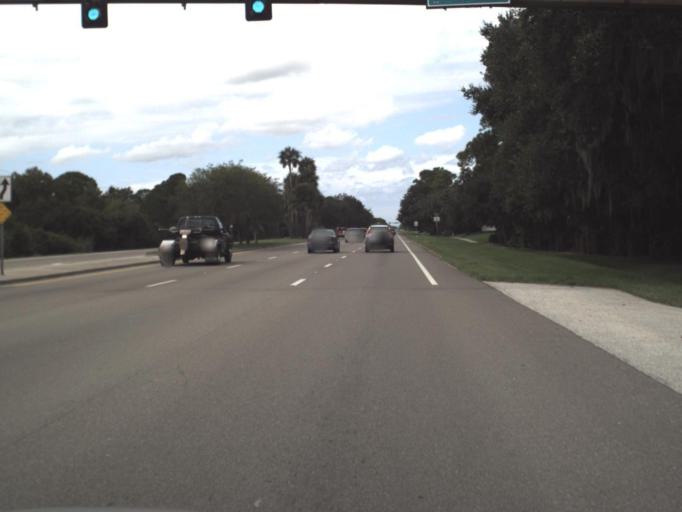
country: US
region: Florida
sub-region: Sarasota County
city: Desoto Lakes
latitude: 27.3884
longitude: -82.4722
